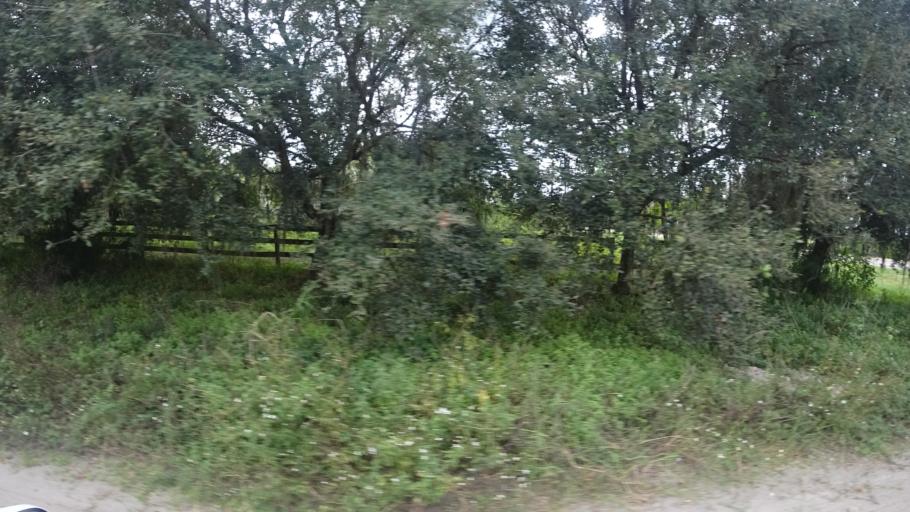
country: US
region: Florida
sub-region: Sarasota County
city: Lake Sarasota
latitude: 27.3867
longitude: -82.2503
